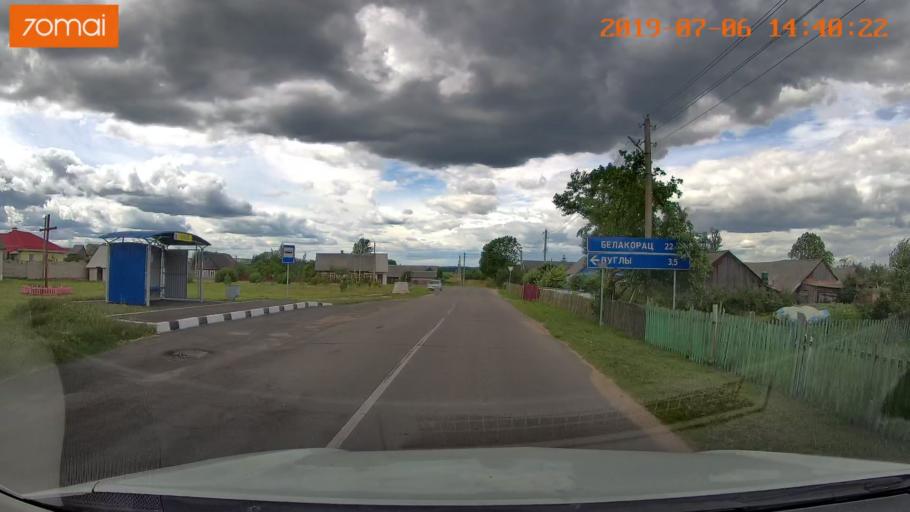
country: BY
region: Minsk
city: Ivyanyets
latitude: 53.9240
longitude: 26.6737
